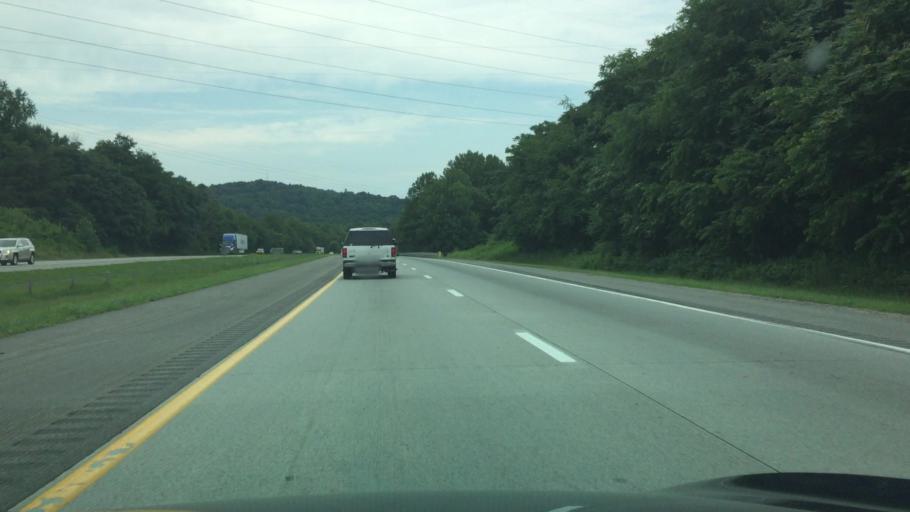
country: US
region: North Carolina
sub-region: Yadkin County
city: Jonesville
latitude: 36.1729
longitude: -80.8096
